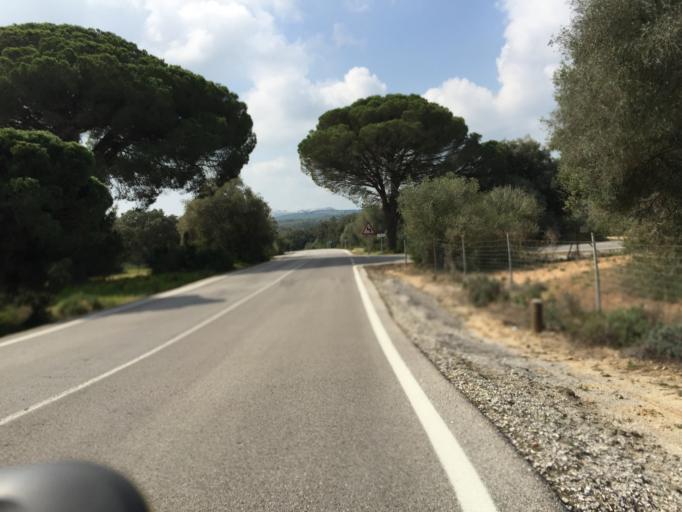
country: ES
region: Andalusia
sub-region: Provincia de Cadiz
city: Vejer de la Frontera
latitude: 36.2903
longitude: -5.9320
